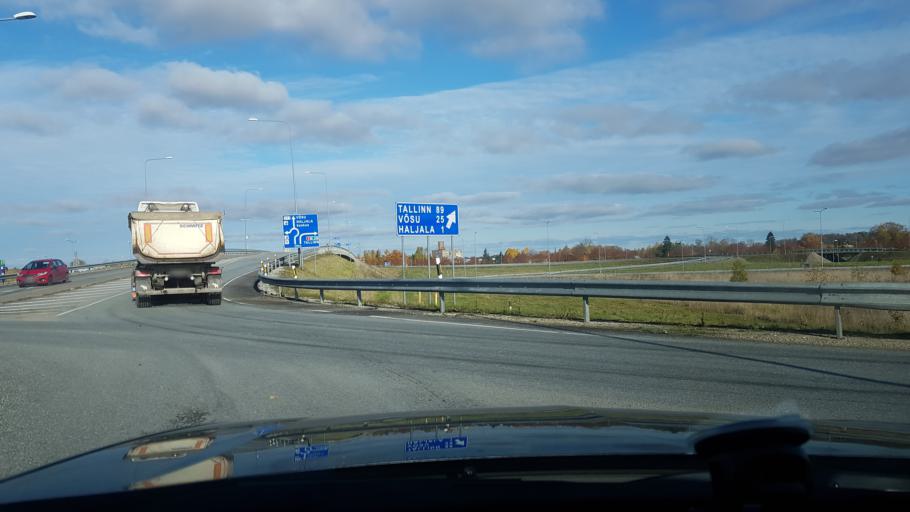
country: EE
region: Laeaene-Virumaa
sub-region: Haljala vald
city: Haljala
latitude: 59.4225
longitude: 26.2698
